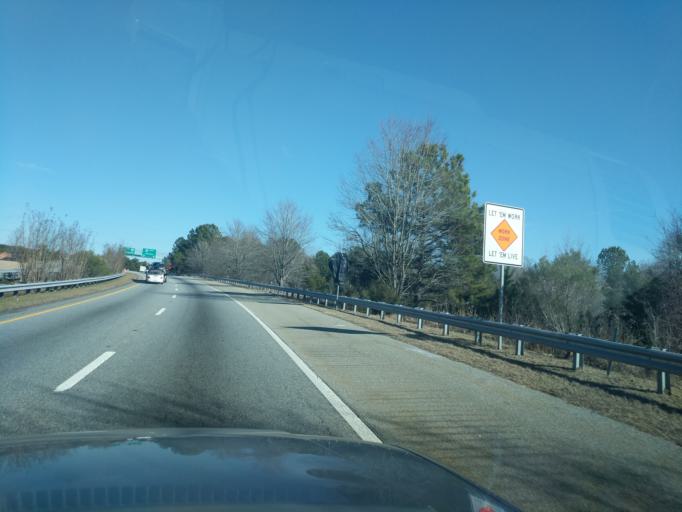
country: US
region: South Carolina
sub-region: Spartanburg County
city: Valley Falls
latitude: 35.0069
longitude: -81.9173
